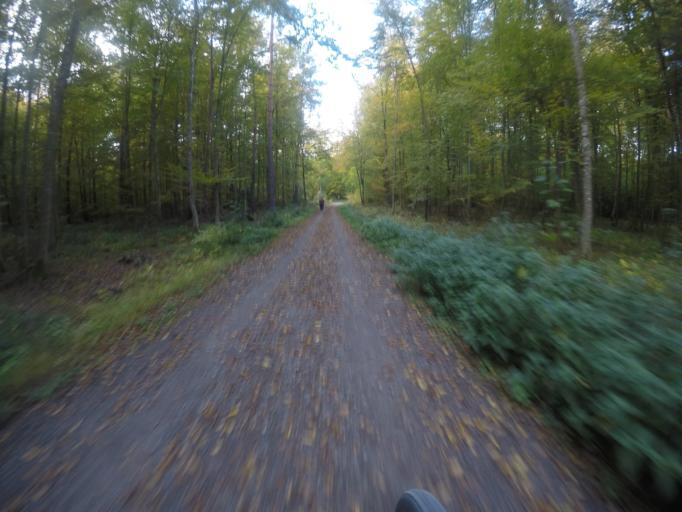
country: DE
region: Baden-Wuerttemberg
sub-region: Regierungsbezirk Stuttgart
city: Weil im Schonbuch
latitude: 48.6091
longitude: 9.0487
